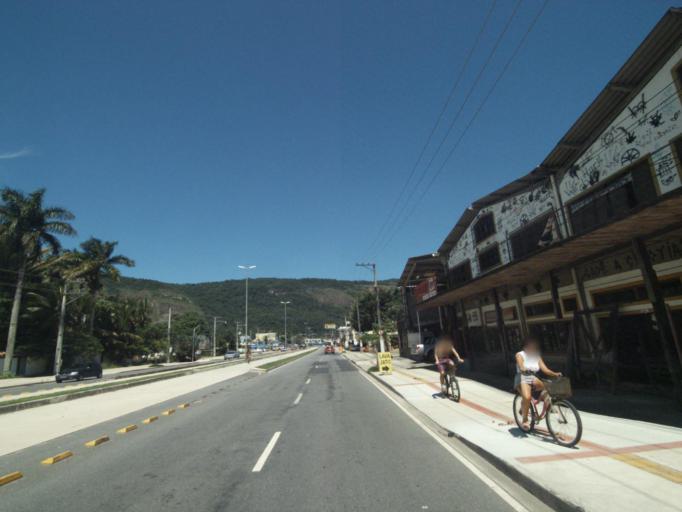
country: BR
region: Rio de Janeiro
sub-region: Niteroi
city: Niteroi
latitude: -22.9499
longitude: -43.0296
